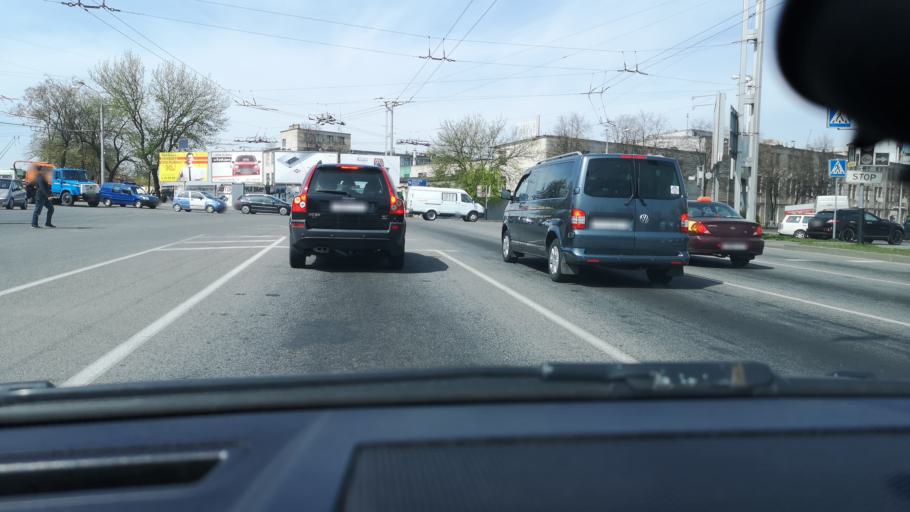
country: BY
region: Gomel
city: Gomel
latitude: 52.4160
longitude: 31.0006
